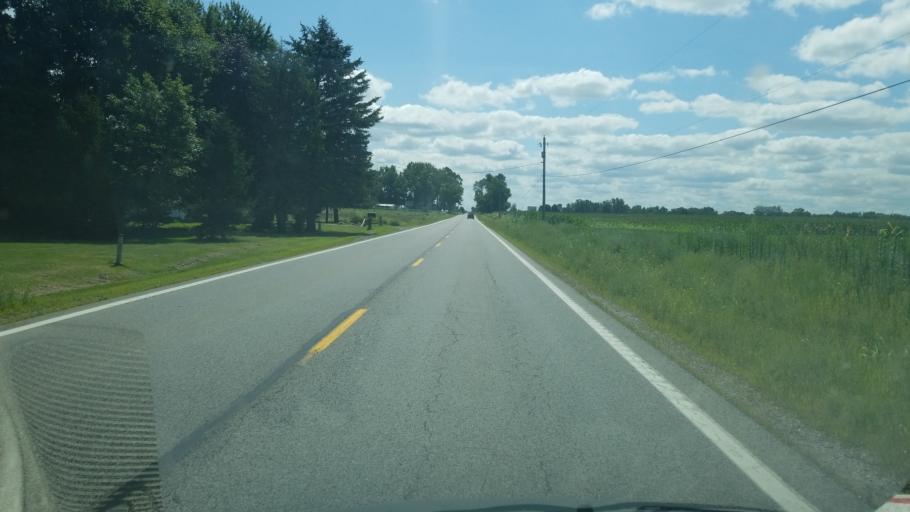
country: US
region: Ohio
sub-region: Fulton County
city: Delta
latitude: 41.6136
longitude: -84.0375
